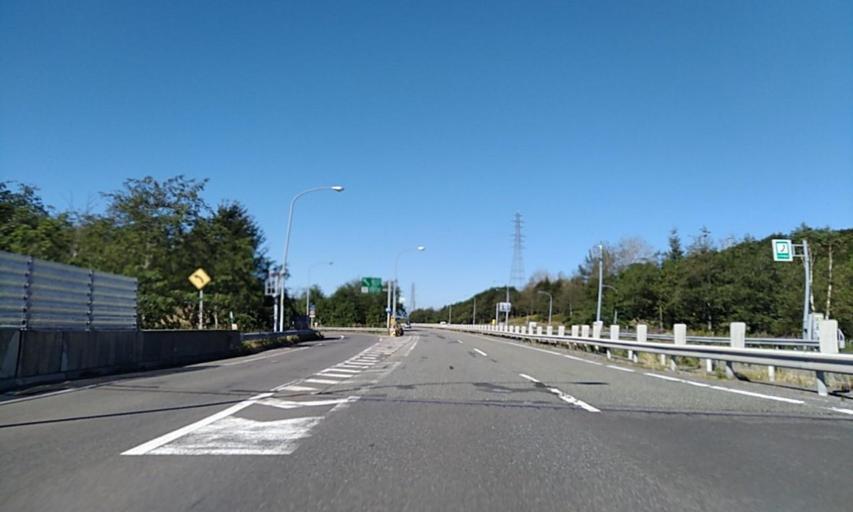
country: JP
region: Hokkaido
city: Tomakomai
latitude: 42.6726
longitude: 141.7838
